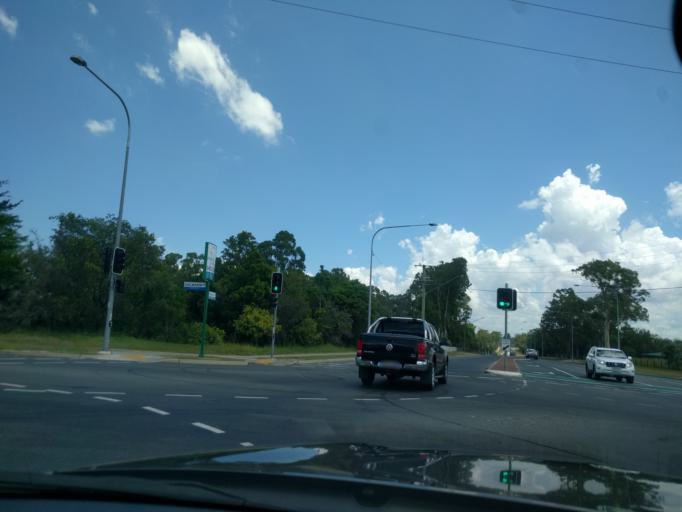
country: AU
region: Queensland
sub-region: Moreton Bay
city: Burpengary
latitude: -27.1391
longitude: 152.9821
